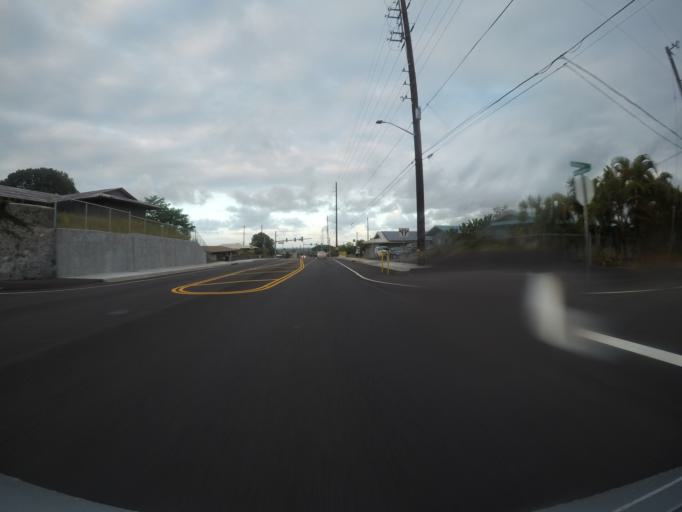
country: US
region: Hawaii
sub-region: Hawaii County
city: Hilo
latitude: 19.6836
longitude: -155.0831
